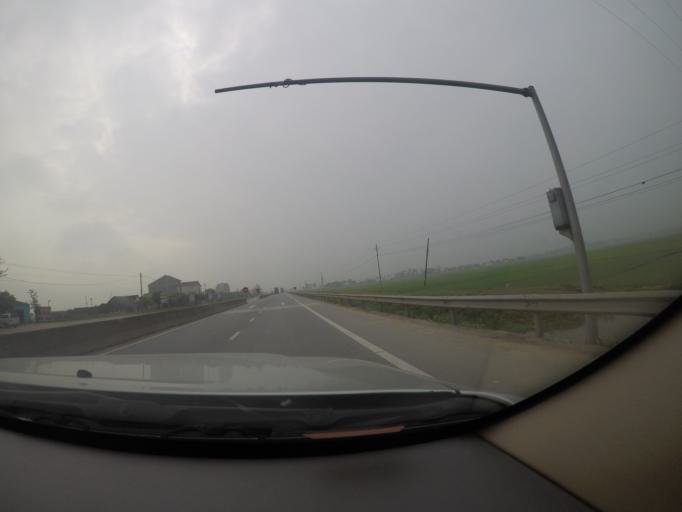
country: VN
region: Ha Tinh
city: Ky Anh
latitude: 18.1855
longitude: 106.1944
